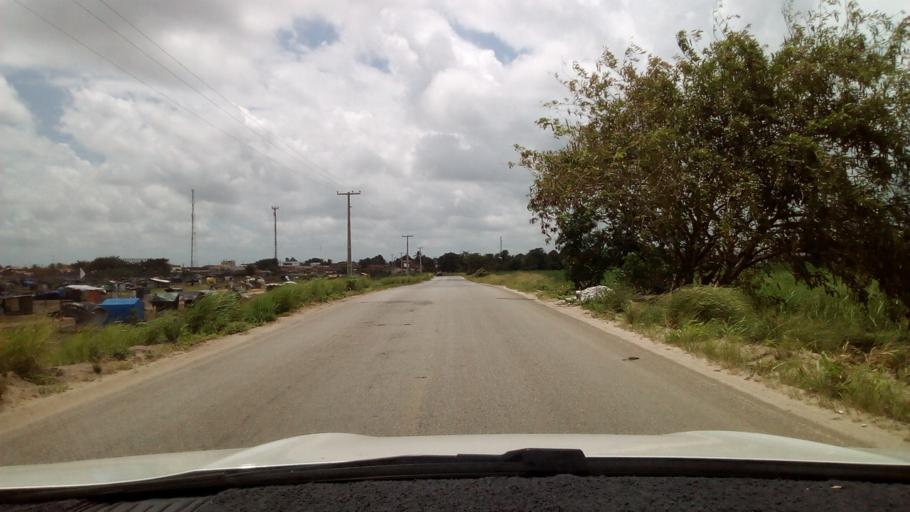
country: BR
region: Paraiba
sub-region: Caapora
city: Caapora
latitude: -7.5078
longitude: -34.9173
